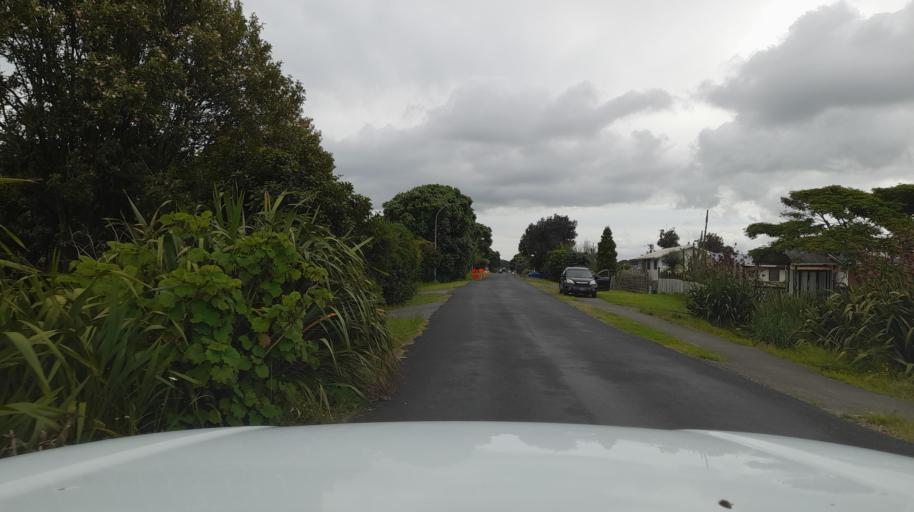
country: NZ
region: Northland
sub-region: Far North District
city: Ahipara
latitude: -35.1658
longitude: 173.1546
